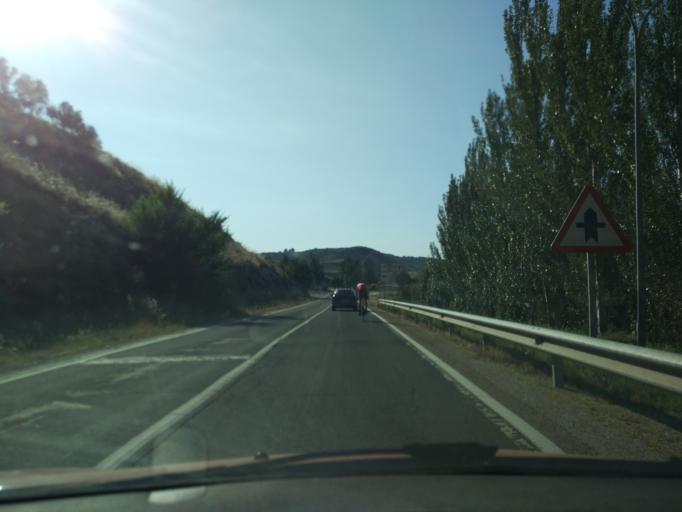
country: ES
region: Madrid
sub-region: Provincia de Madrid
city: Valverde de Alcala
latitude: 40.4158
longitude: -3.2982
